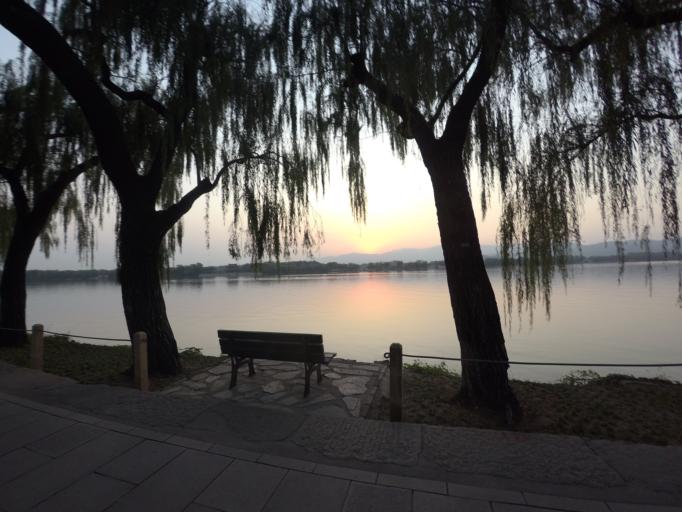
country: CN
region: Beijing
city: Haidian
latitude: 39.9871
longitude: 116.2722
